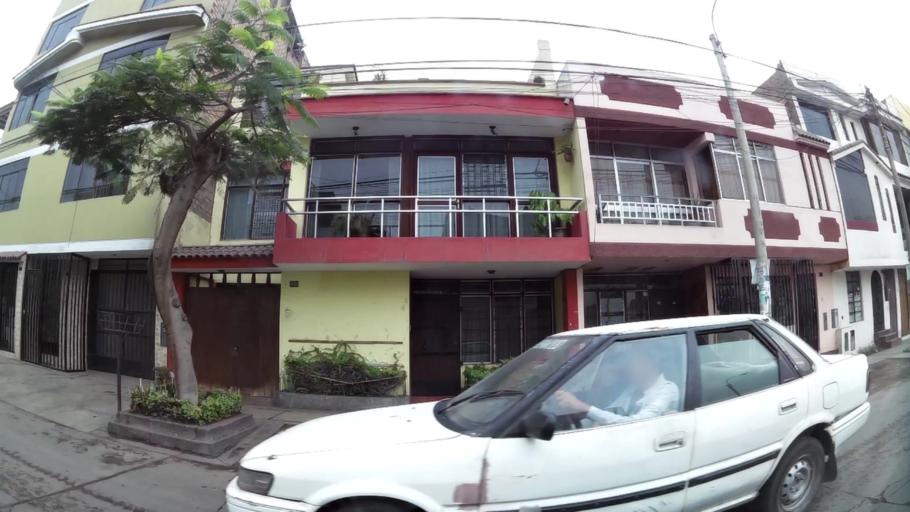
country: PE
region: Lima
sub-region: Lima
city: San Luis
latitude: -12.0719
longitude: -77.0082
